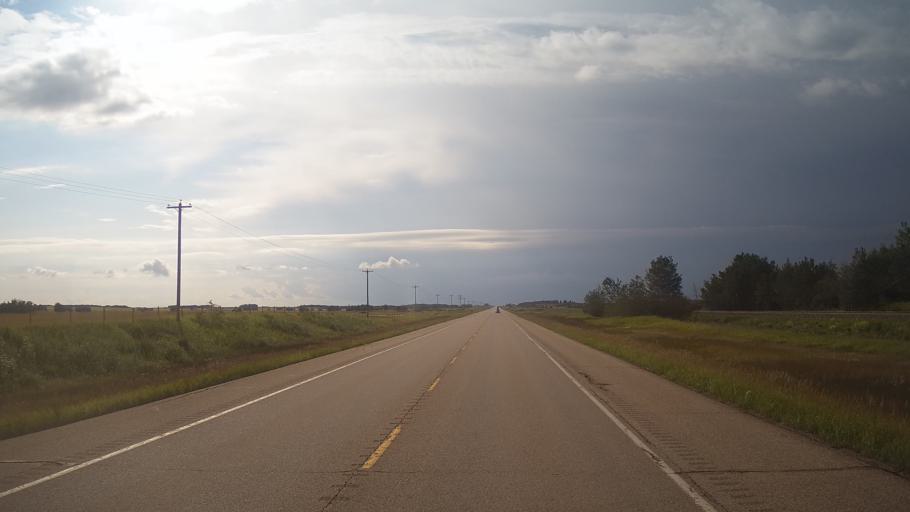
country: CA
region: Alberta
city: Viking
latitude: 53.1508
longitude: -111.9715
